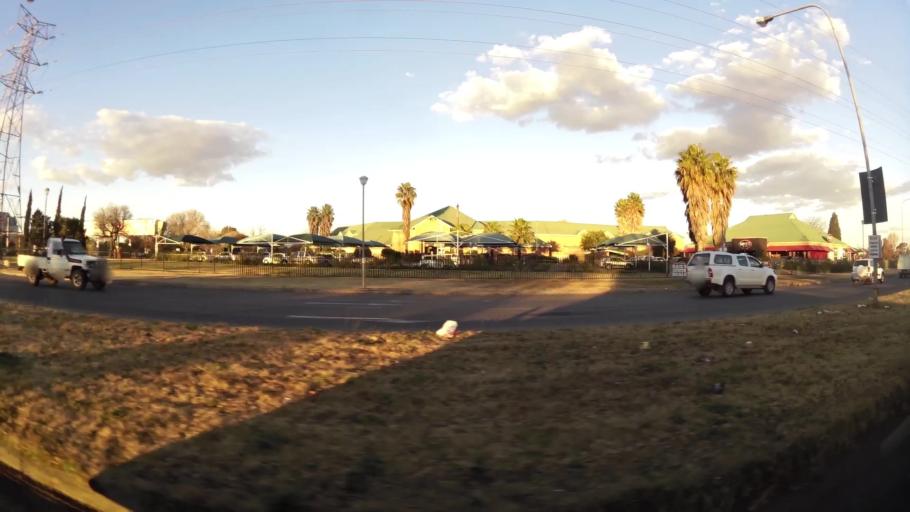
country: ZA
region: North-West
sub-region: Dr Kenneth Kaunda District Municipality
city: Potchefstroom
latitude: -26.7158
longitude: 27.1031
